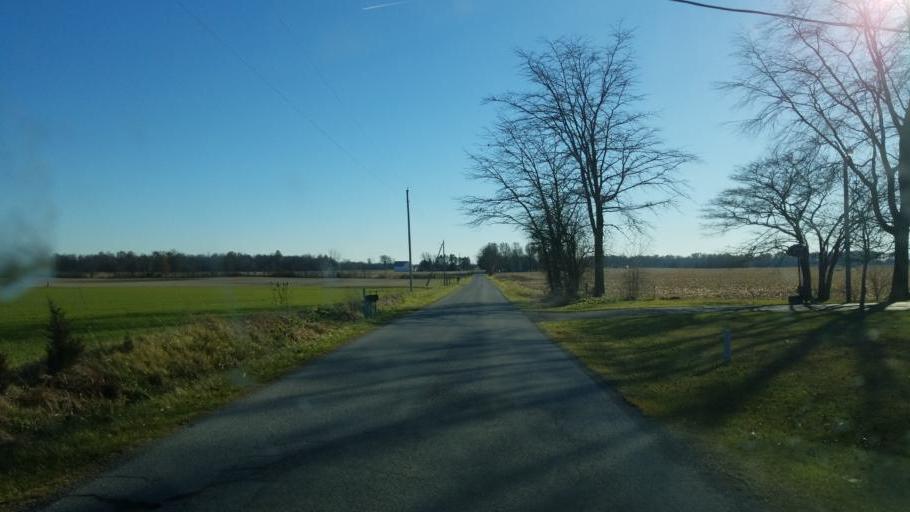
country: US
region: Ohio
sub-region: Morrow County
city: Cardington
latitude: 40.5318
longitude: -82.9484
